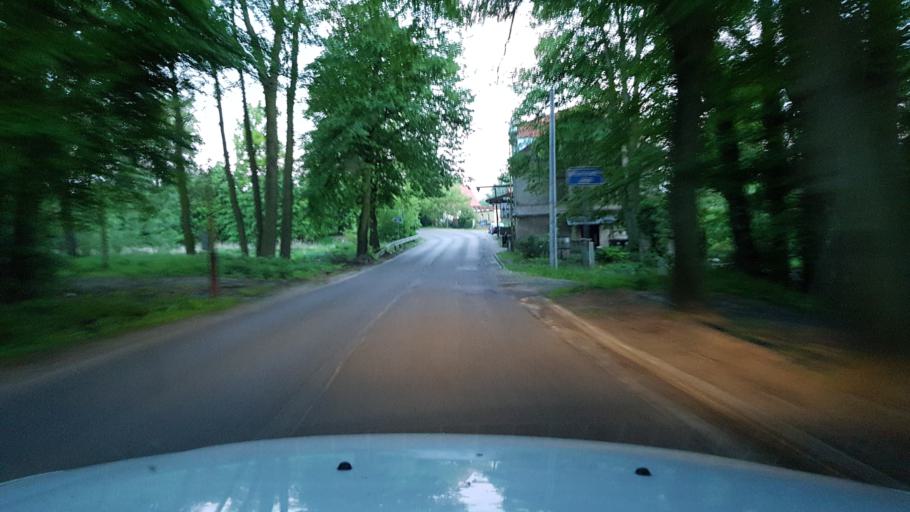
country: PL
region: West Pomeranian Voivodeship
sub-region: Powiat goleniowski
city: Goleniow
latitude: 53.5541
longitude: 14.8529
